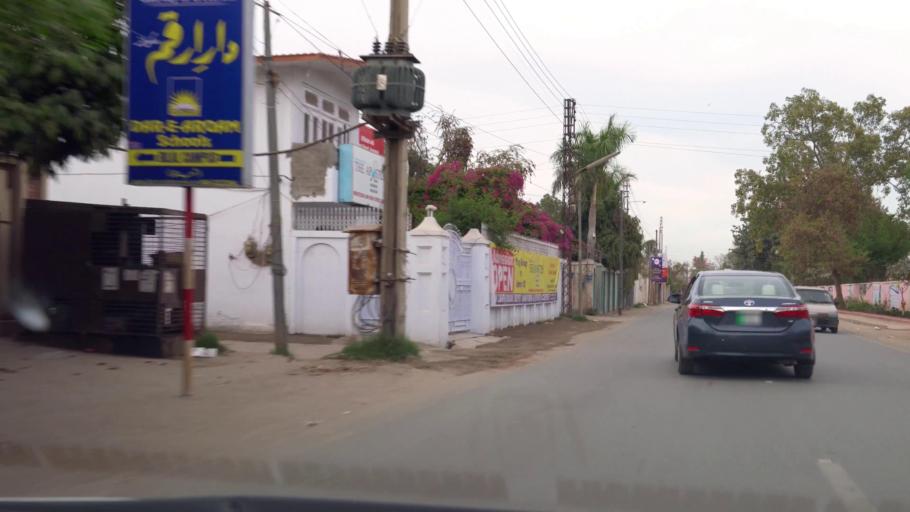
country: PK
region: Punjab
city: Sargodha
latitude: 32.0741
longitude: 72.6781
